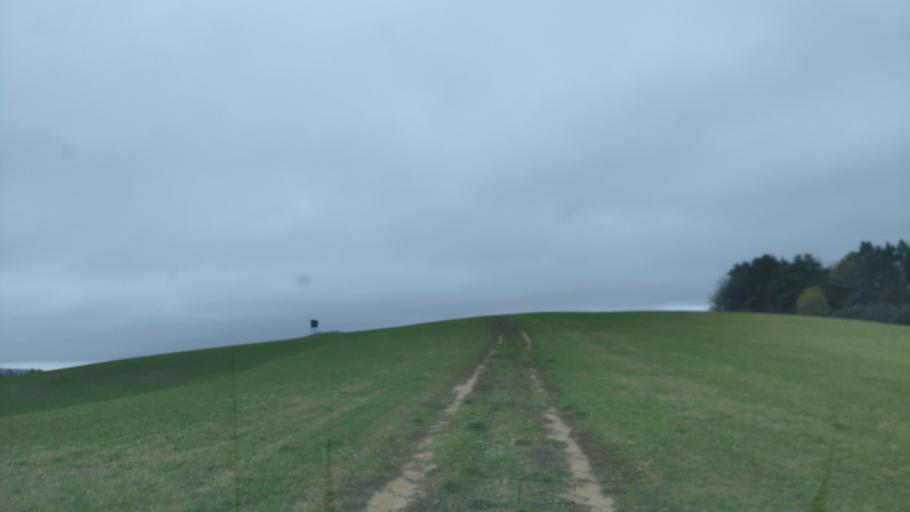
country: SK
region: Presovsky
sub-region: Okres Presov
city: Presov
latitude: 48.9359
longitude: 21.1049
